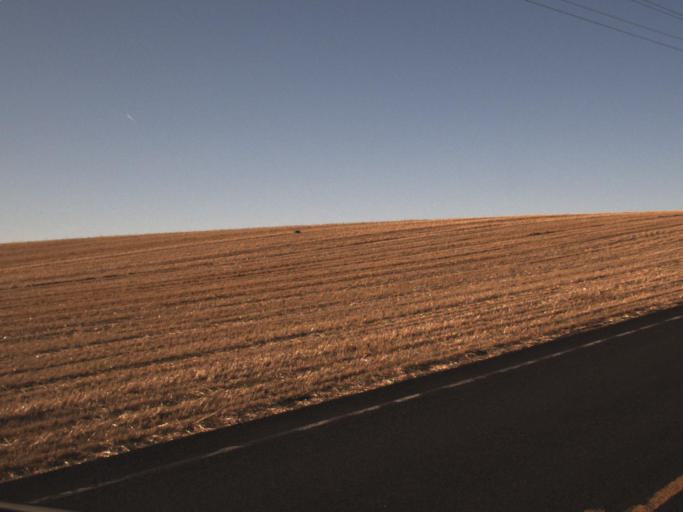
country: US
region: Washington
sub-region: Adams County
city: Ritzville
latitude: 47.0551
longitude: -118.3609
